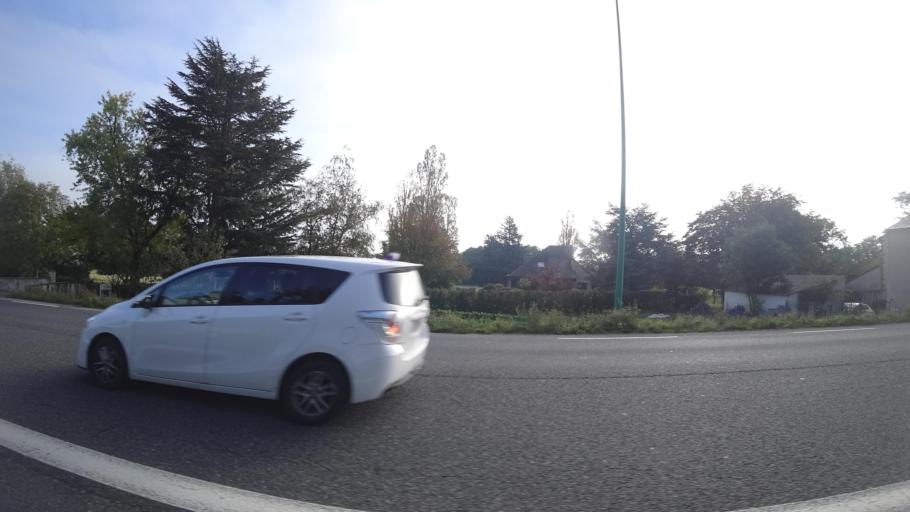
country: FR
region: Midi-Pyrenees
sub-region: Departement de l'Aveyron
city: Luc-la-Primaube
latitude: 44.3070
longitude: 2.5572
